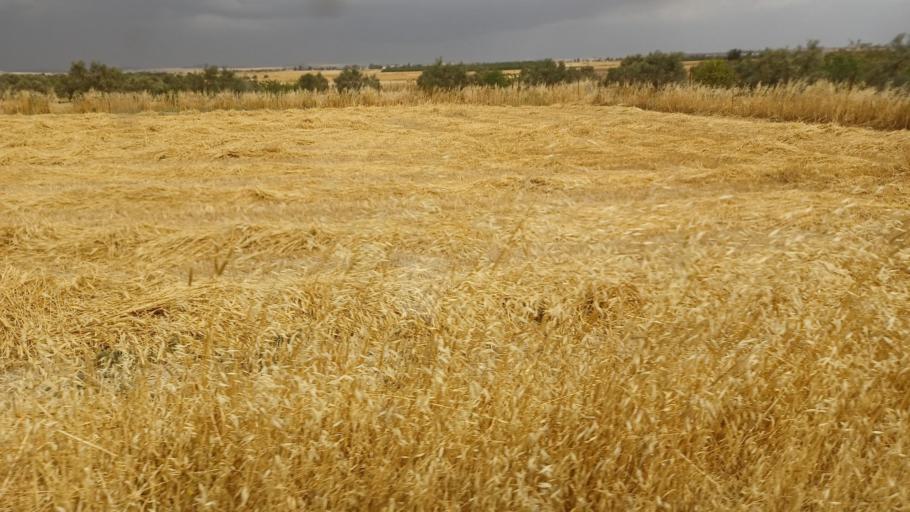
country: CY
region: Larnaka
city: Athienou
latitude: 35.0754
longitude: 33.5248
